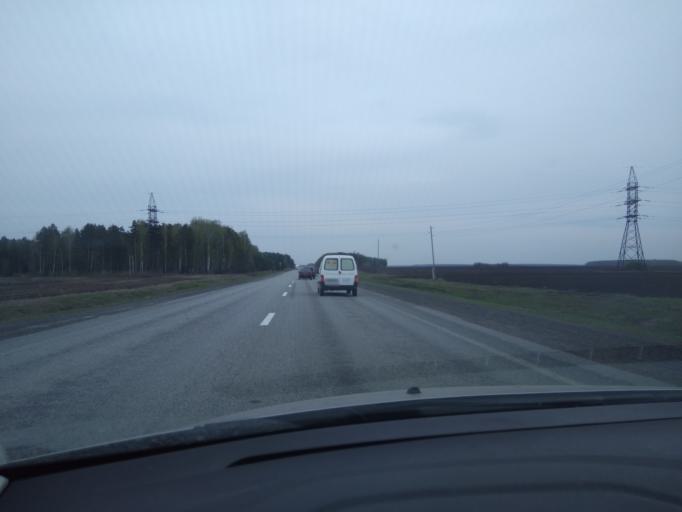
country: RU
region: Sverdlovsk
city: Gryaznovskoye
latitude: 56.7813
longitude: 61.6139
